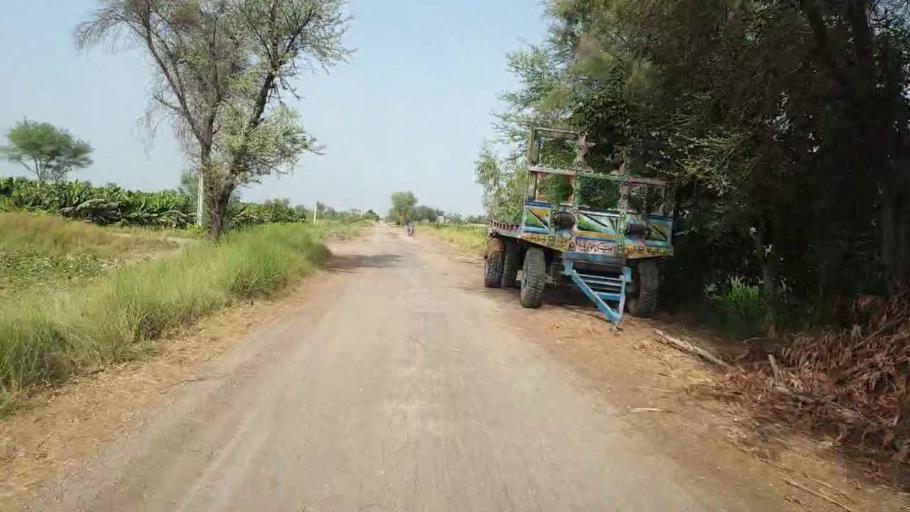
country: PK
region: Sindh
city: Daur
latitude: 26.3227
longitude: 68.1611
